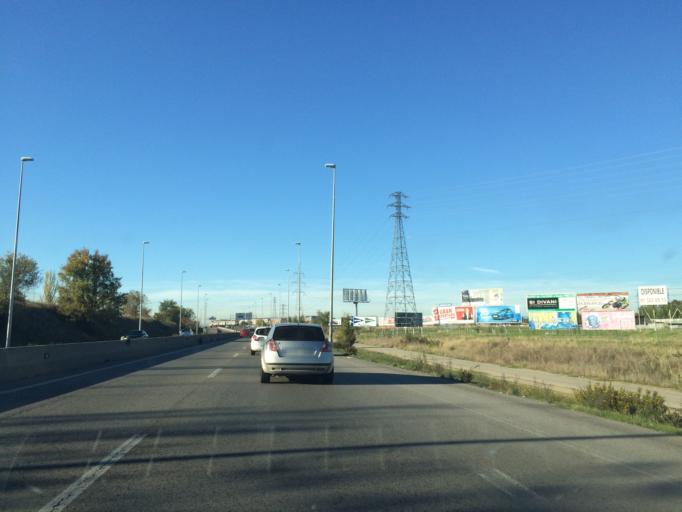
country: ES
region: Madrid
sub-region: Provincia de Madrid
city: Mostoles
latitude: 40.3271
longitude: -3.8485
